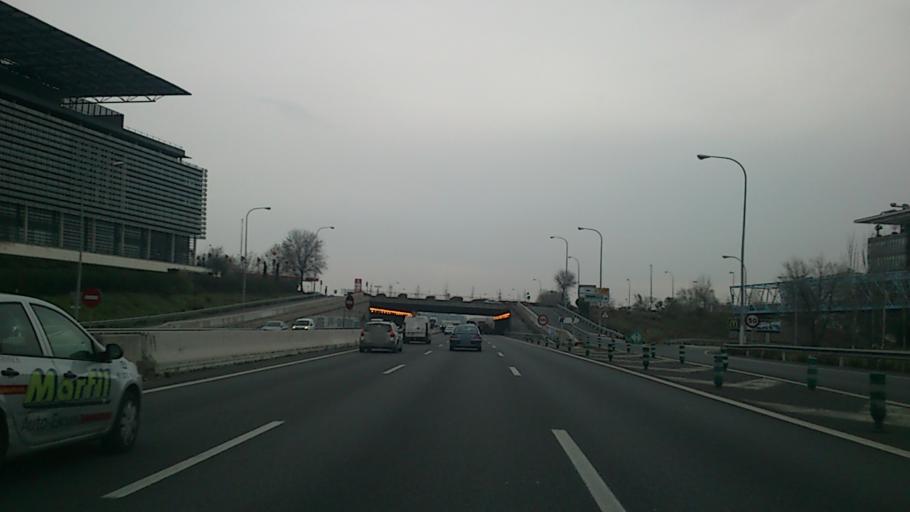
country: ES
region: Madrid
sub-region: Provincia de Madrid
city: San Blas
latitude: 40.4595
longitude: -3.6199
